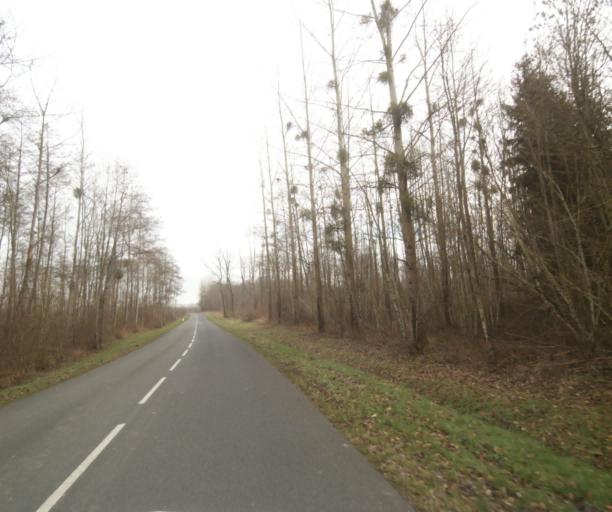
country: FR
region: Champagne-Ardenne
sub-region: Departement de la Marne
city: Pargny-sur-Saulx
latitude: 48.7409
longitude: 4.8644
